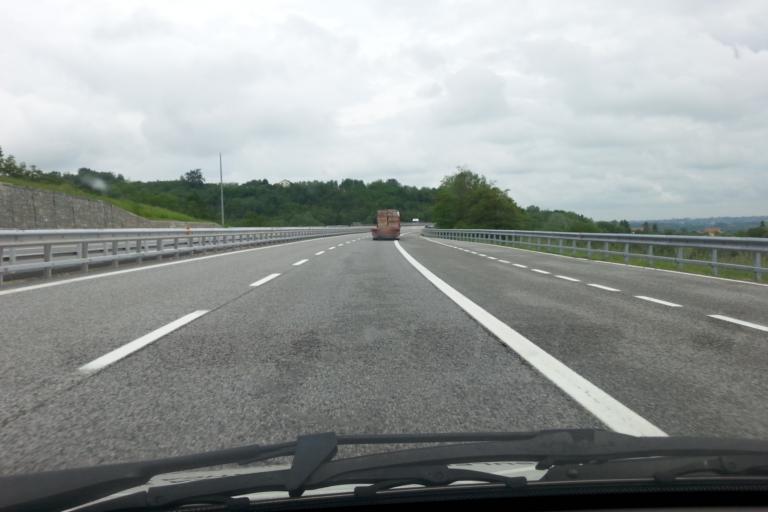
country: IT
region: Piedmont
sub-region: Provincia di Cuneo
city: Bastia Mondovi
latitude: 44.4173
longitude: 7.8943
